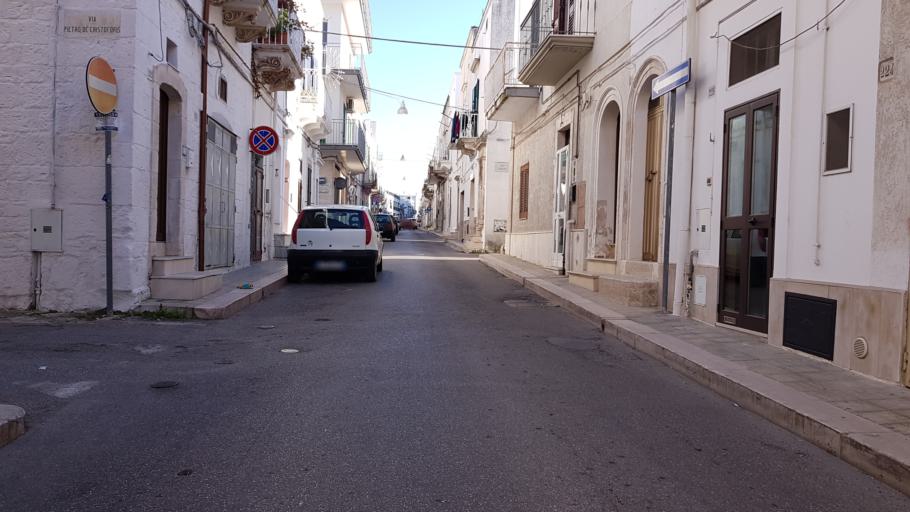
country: IT
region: Apulia
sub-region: Provincia di Brindisi
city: Ostuni
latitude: 40.7272
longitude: 17.5807
